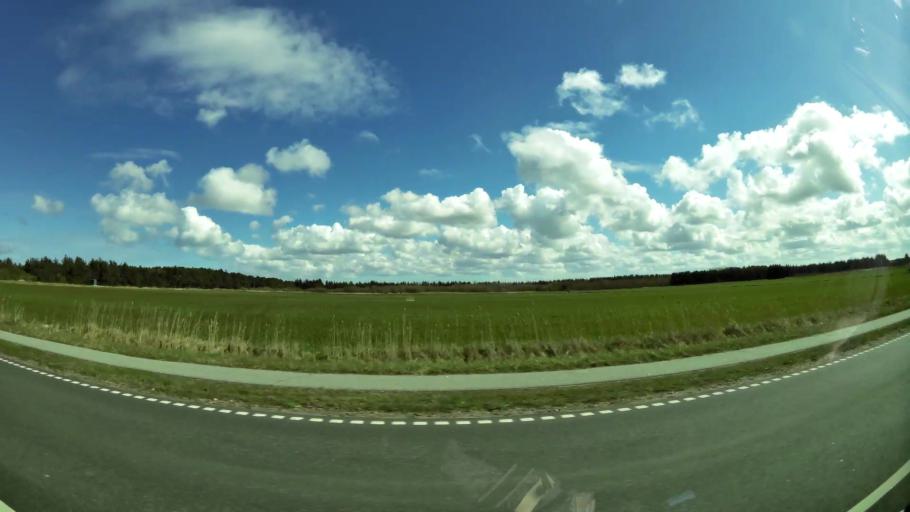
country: DK
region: North Denmark
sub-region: Hjorring Kommune
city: Hirtshals
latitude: 57.5600
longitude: 9.9391
